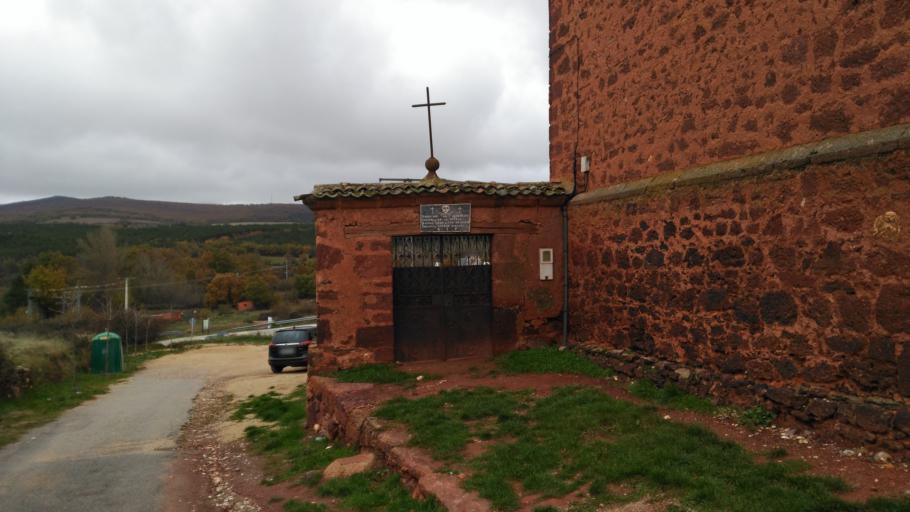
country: ES
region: Castille and Leon
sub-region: Provincia de Soria
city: Liceras
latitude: 41.3137
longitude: -3.3310
